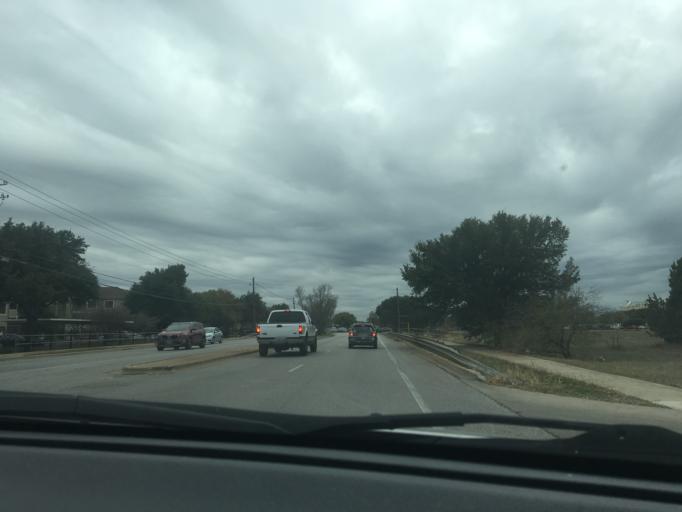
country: US
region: Texas
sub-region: Travis County
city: Shady Hollow
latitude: 30.2177
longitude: -97.8281
